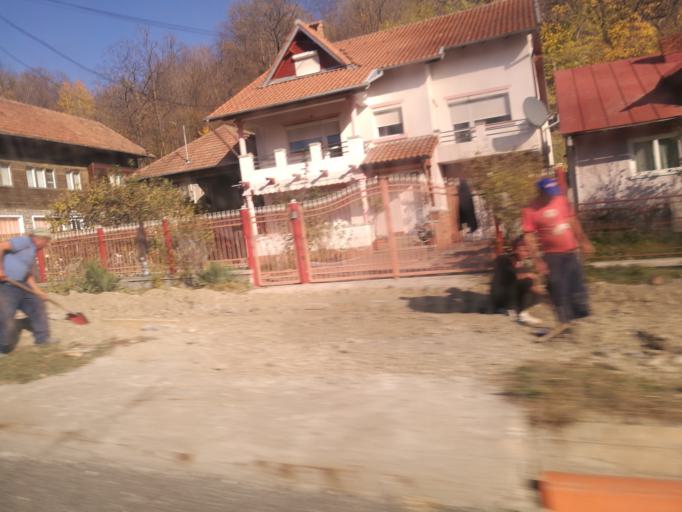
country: RO
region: Prahova
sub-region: Comuna Comarnic
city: Comarnic
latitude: 45.2539
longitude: 25.6291
